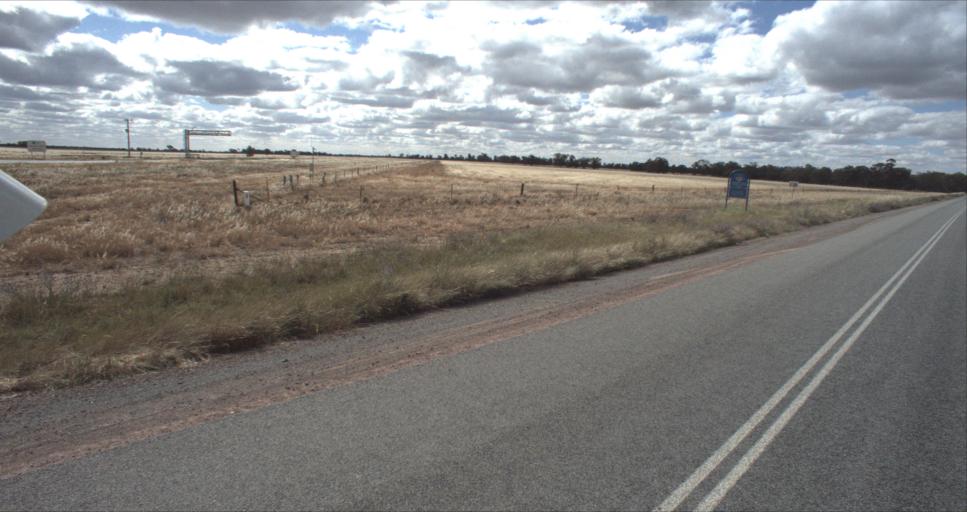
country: AU
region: New South Wales
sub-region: Leeton
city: Leeton
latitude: -34.6969
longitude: 146.3427
